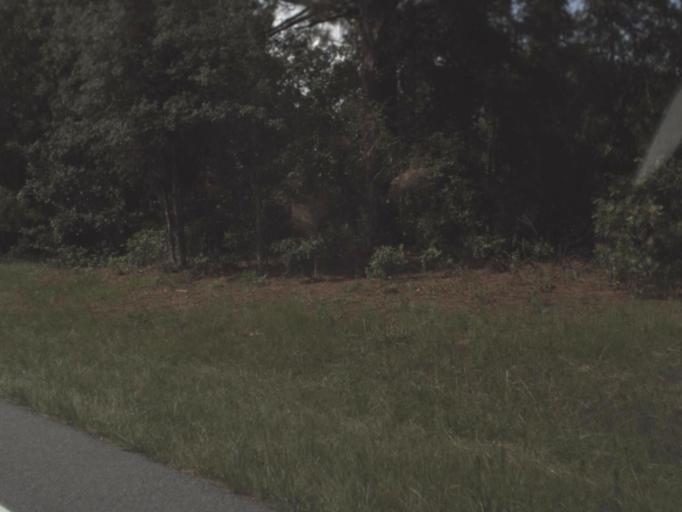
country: US
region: Florida
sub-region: Citrus County
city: Citrus Springs
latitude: 28.9864
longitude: -82.4351
